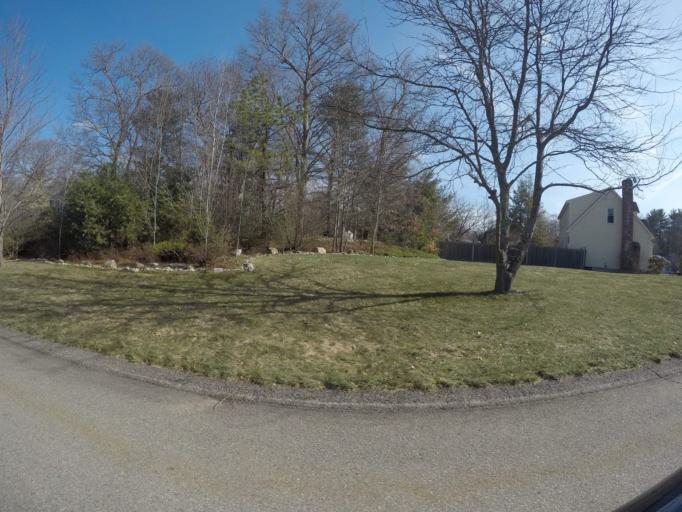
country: US
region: Massachusetts
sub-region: Bristol County
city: Easton
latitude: 42.0179
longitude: -71.1630
